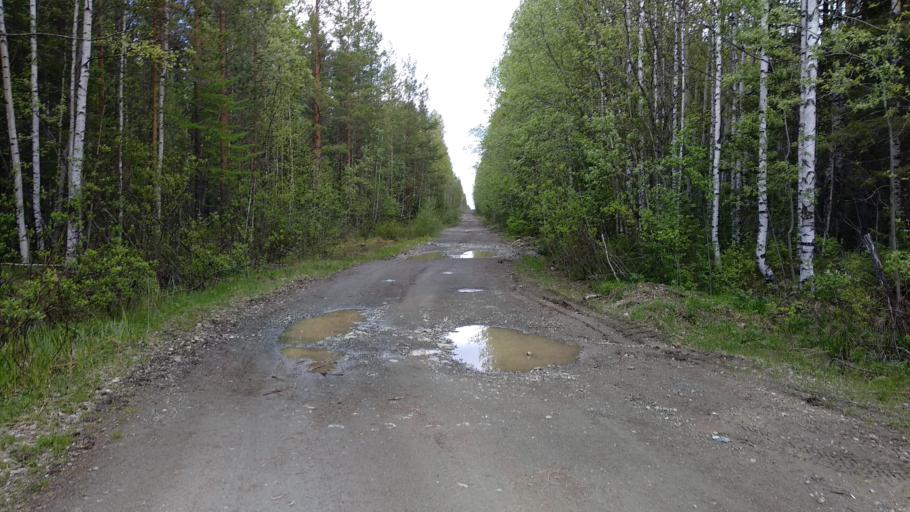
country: RU
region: Sverdlovsk
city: Karpinsk
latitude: 59.8684
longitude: 59.5392
